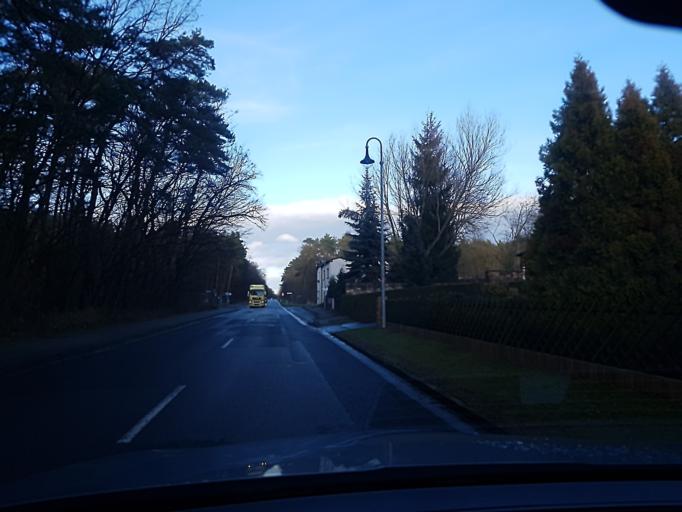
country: DE
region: Brandenburg
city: Trobitz
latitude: 51.5748
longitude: 13.4277
